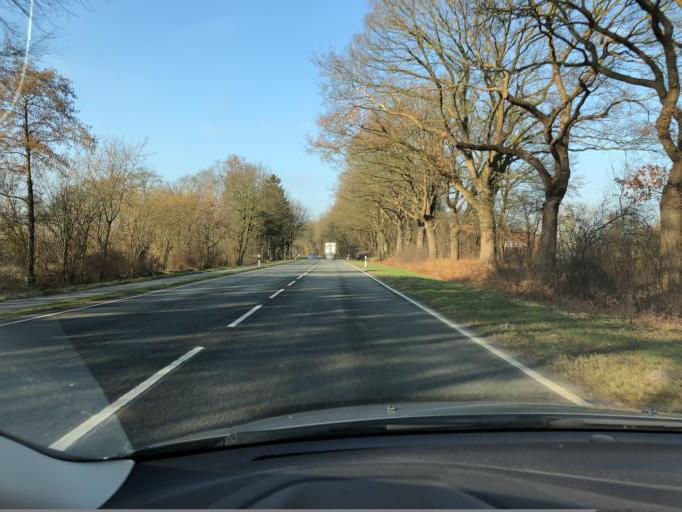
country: DE
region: Lower Saxony
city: Westerstede
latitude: 53.2925
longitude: 7.8726
